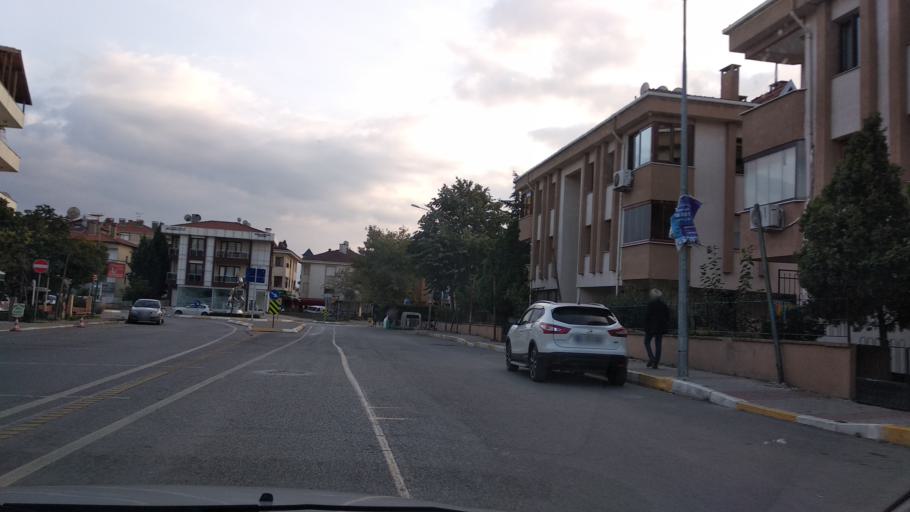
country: TR
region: Istanbul
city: Icmeler
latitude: 40.8207
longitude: 29.2994
